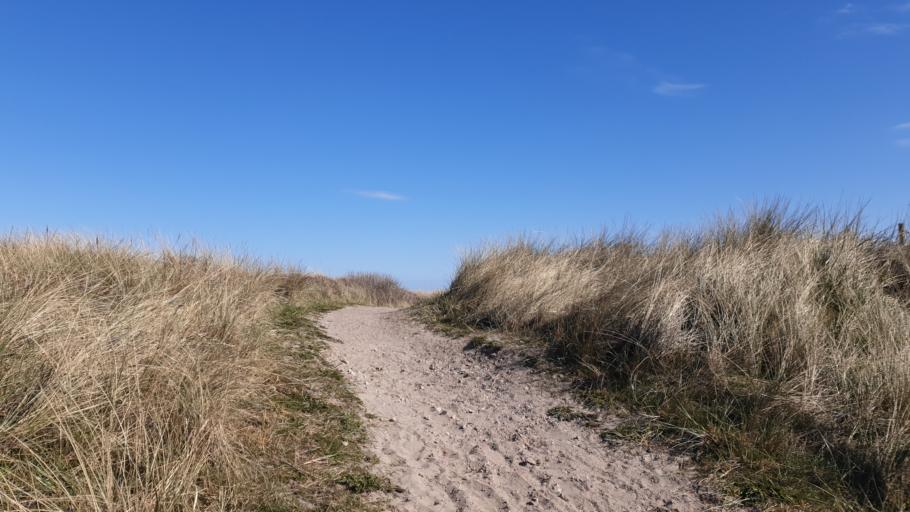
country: DK
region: North Denmark
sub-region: Hjorring Kommune
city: Hjorring
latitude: 57.4960
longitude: 9.8345
